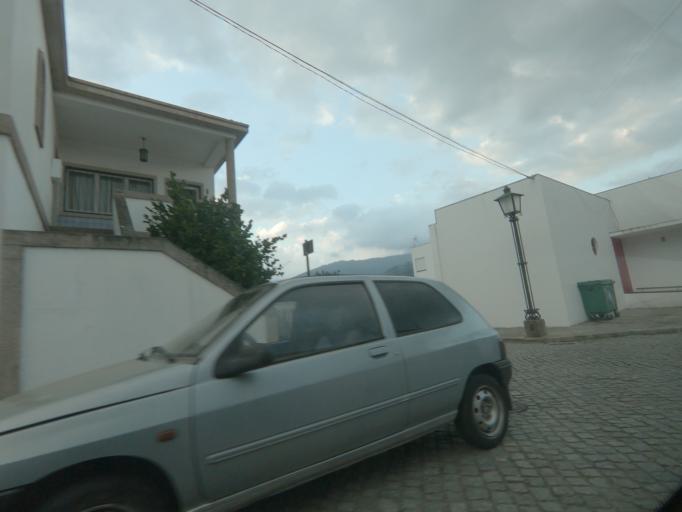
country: PT
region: Vila Real
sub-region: Mesao Frio
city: Mesao Frio
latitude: 41.1579
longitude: -7.8926
